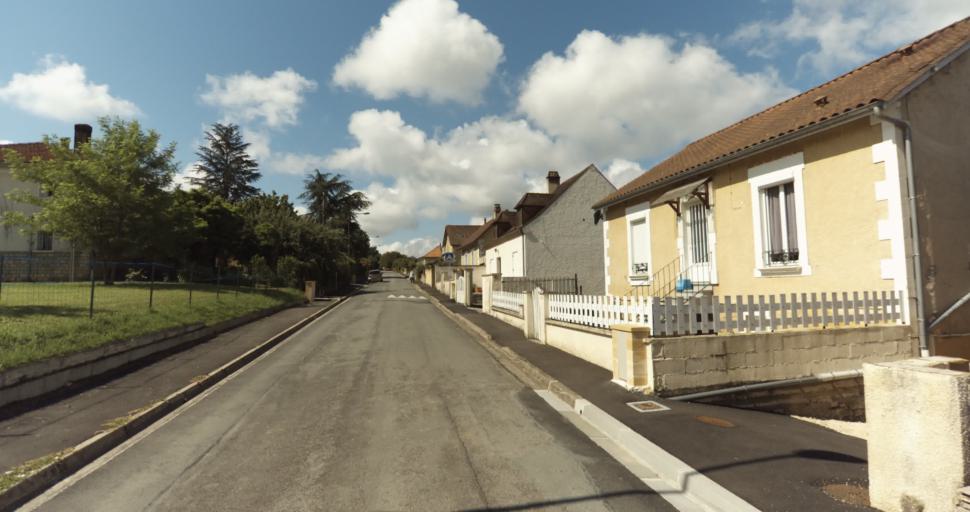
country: FR
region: Aquitaine
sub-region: Departement de la Dordogne
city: Le Bugue
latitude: 44.8450
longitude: 0.9069
